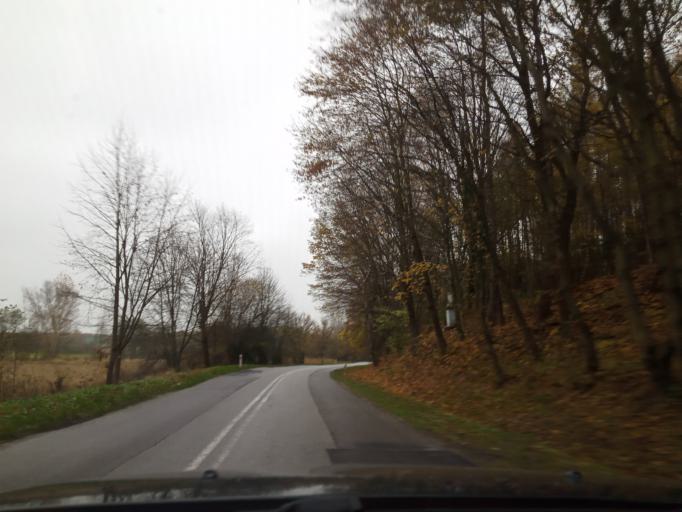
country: PL
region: Swietokrzyskie
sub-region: Powiat pinczowski
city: Dzialoszyce
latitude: 50.4150
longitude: 20.3272
